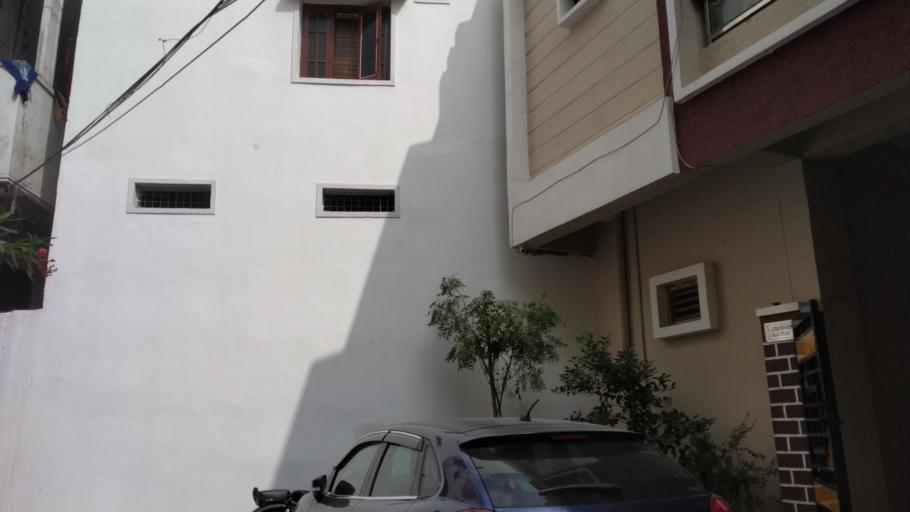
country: IN
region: Telangana
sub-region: Hyderabad
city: Malkajgiri
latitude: 17.4619
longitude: 78.5660
